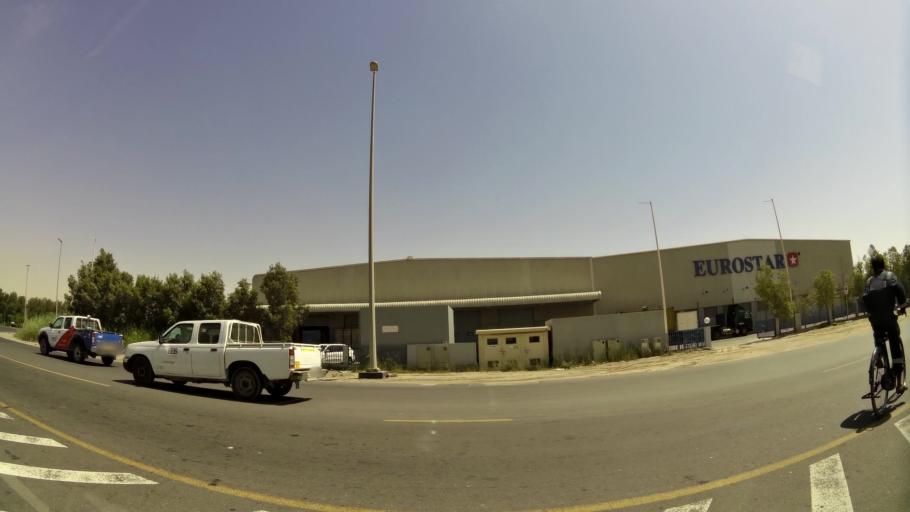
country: AE
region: Dubai
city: Dubai
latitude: 24.9765
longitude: 55.1536
